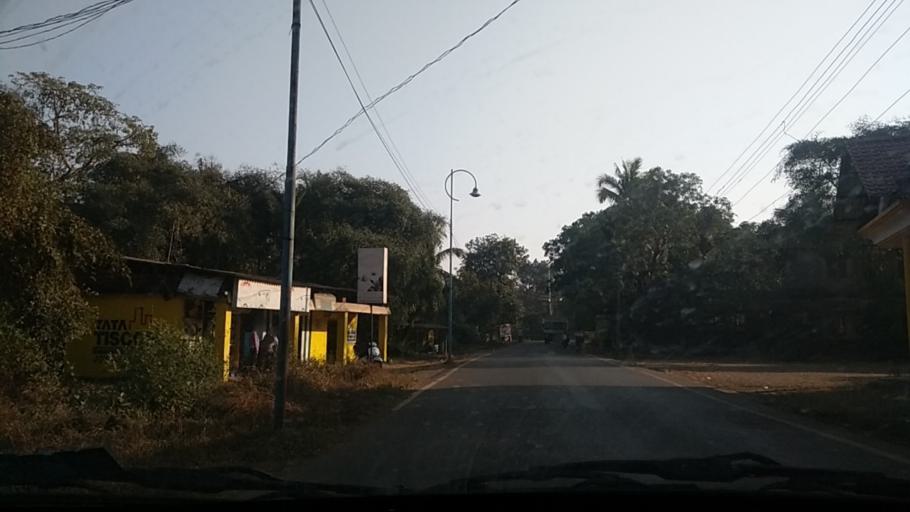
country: IN
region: Goa
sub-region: South Goa
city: Cuncolim
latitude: 15.1842
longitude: 74.0128
